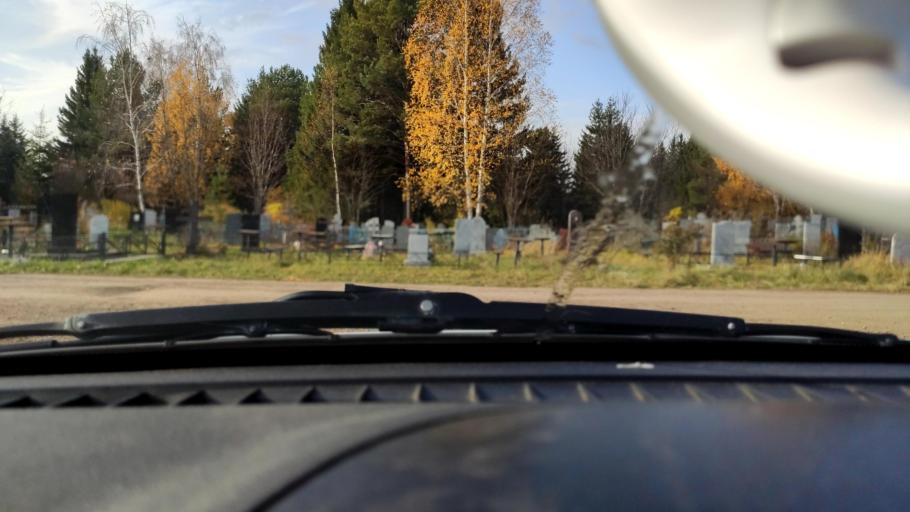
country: RU
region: Perm
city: Kultayevo
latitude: 57.8577
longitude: 55.8691
